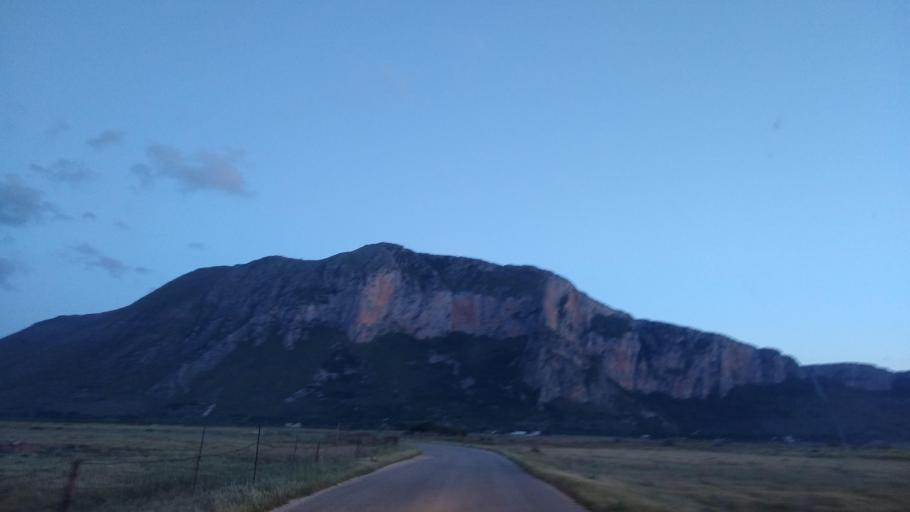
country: IT
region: Sicily
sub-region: Trapani
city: Castelluzzo
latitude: 38.1153
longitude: 12.7204
